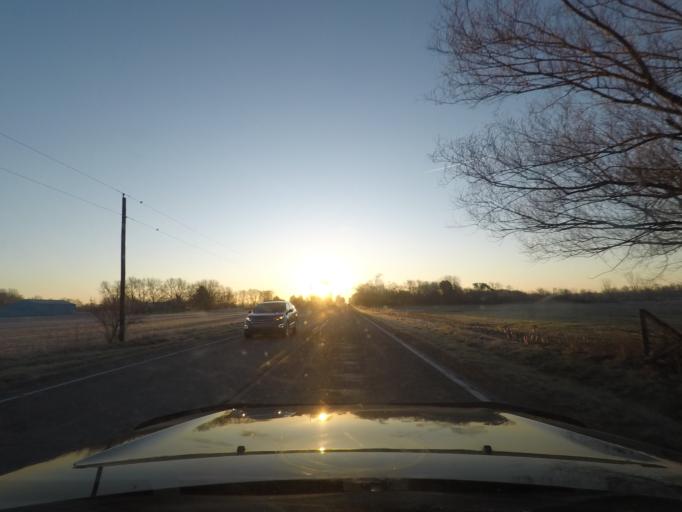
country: US
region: Indiana
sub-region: Saint Joseph County
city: North Liberty
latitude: 41.4485
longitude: -86.3801
